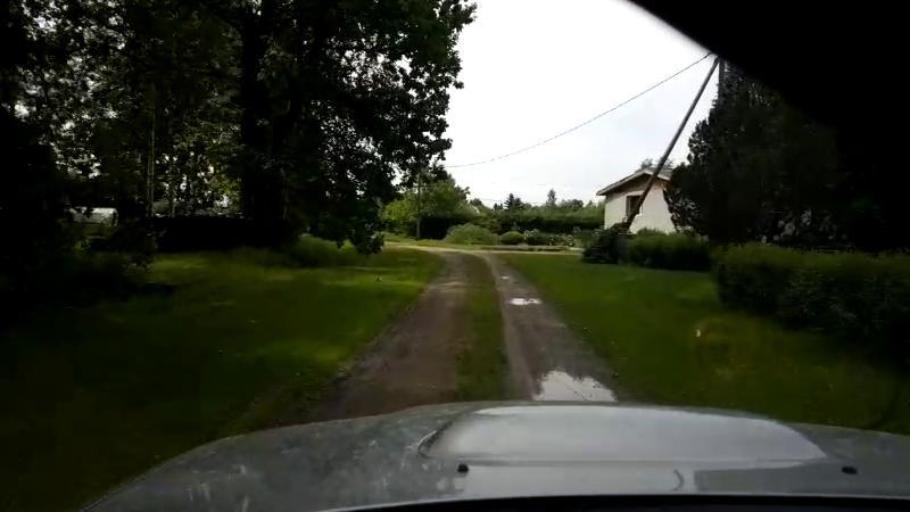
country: EE
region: Paernumaa
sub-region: Tootsi vald
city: Tootsi
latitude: 58.5267
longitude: 24.7082
